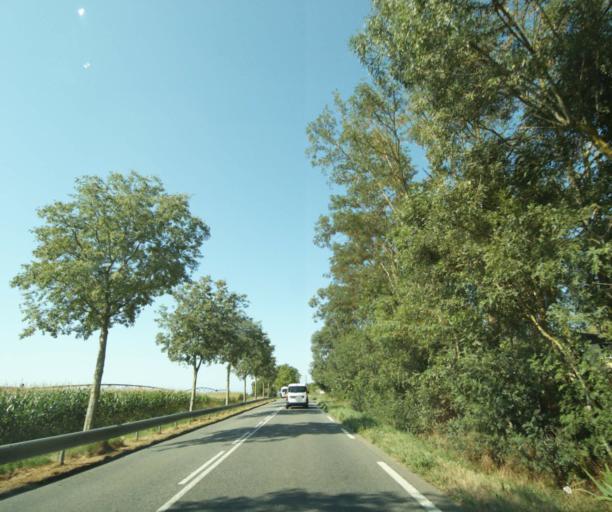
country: FR
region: Midi-Pyrenees
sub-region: Departement de la Haute-Garonne
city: Eaunes
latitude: 43.4023
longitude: 1.3667
